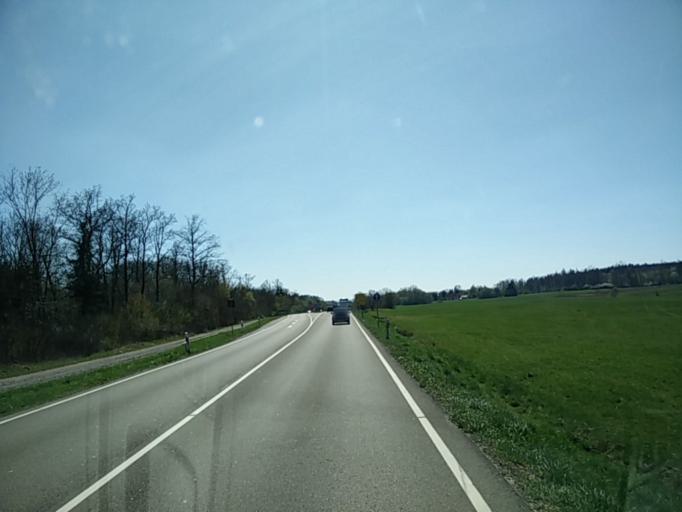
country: DE
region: Baden-Wuerttemberg
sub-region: Tuebingen Region
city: Bodelshausen
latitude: 48.3923
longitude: 9.0006
